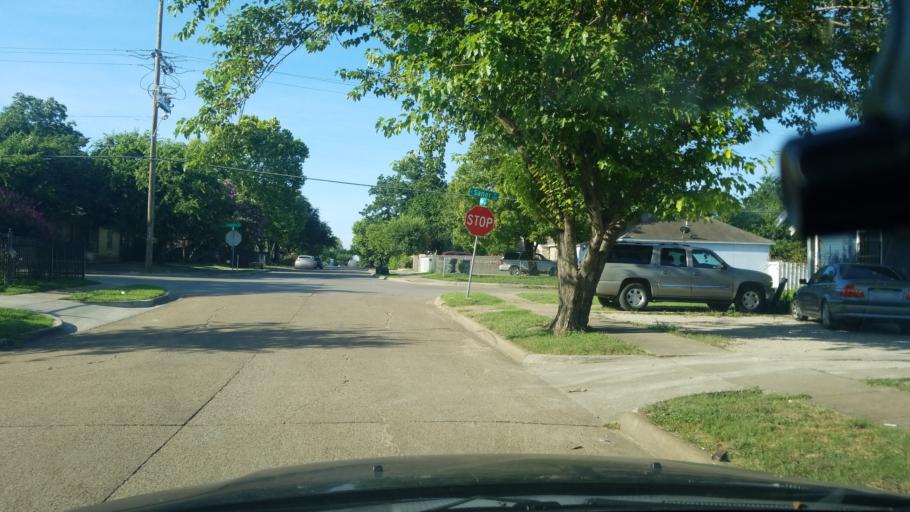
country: US
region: Texas
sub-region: Dallas County
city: Dallas
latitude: 32.7135
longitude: -96.8134
